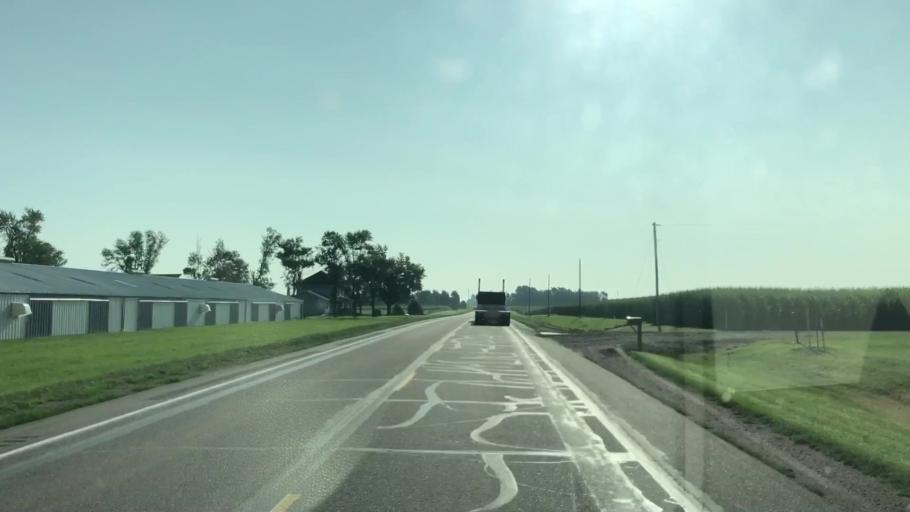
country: US
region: Iowa
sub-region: O'Brien County
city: Sheldon
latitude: 43.1862
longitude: -95.9894
